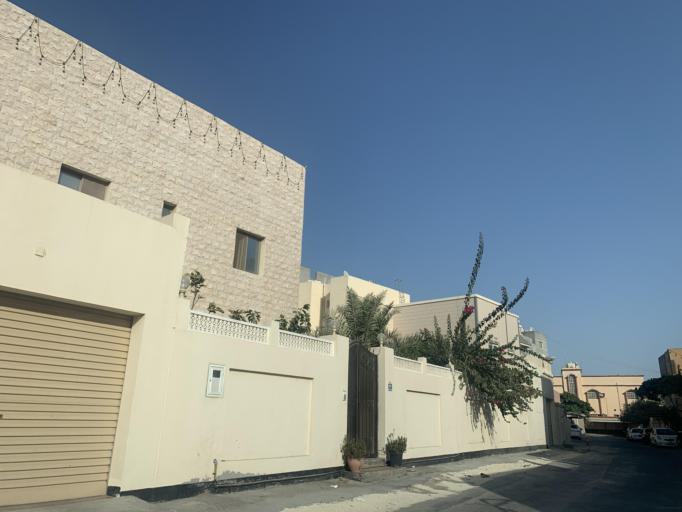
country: BH
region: Muharraq
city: Al Muharraq
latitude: 26.2837
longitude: 50.6326
